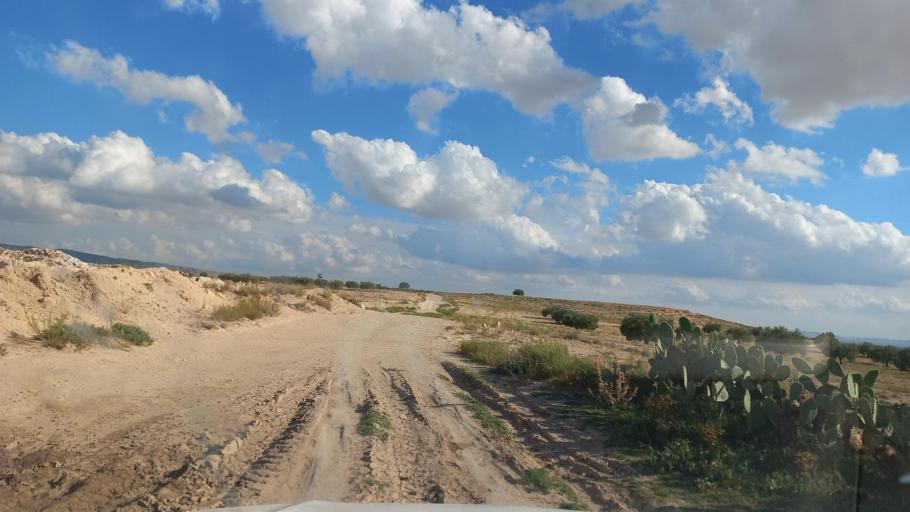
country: TN
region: Al Qasrayn
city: Sbiba
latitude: 35.3961
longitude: 9.0392
